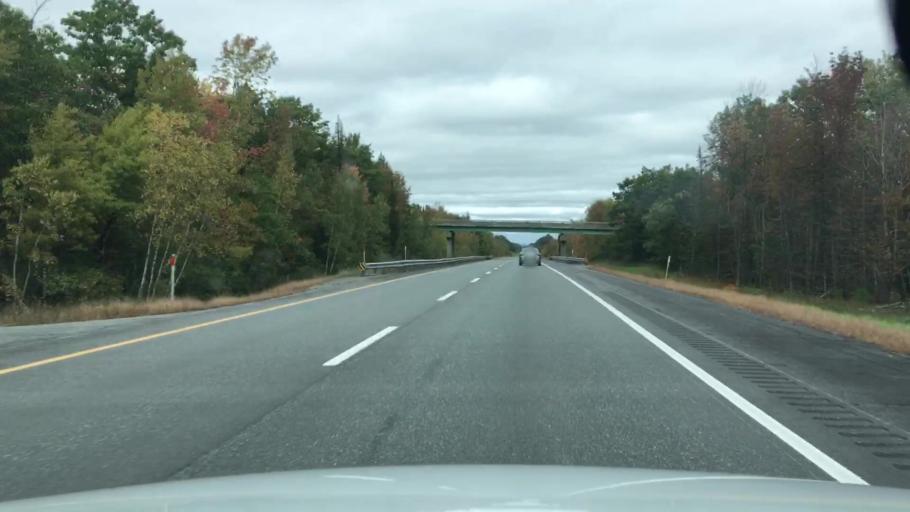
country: US
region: Maine
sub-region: Waldo County
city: Burnham
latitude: 44.7345
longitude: -69.4330
